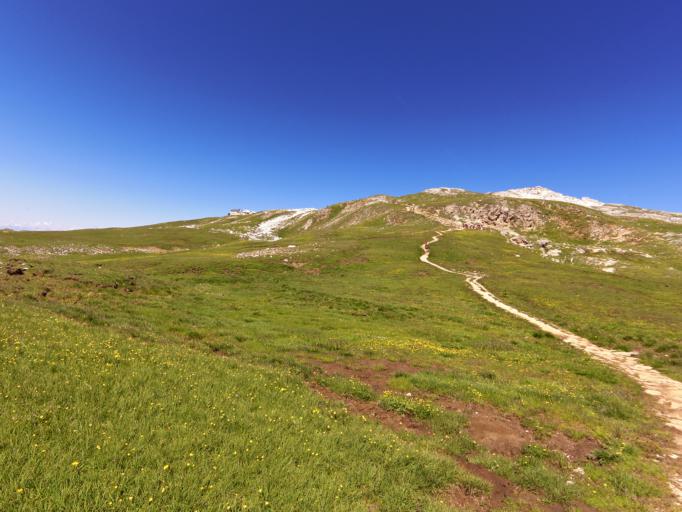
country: IT
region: Trentino-Alto Adige
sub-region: Bolzano
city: Siusi
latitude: 46.5081
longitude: 11.5817
